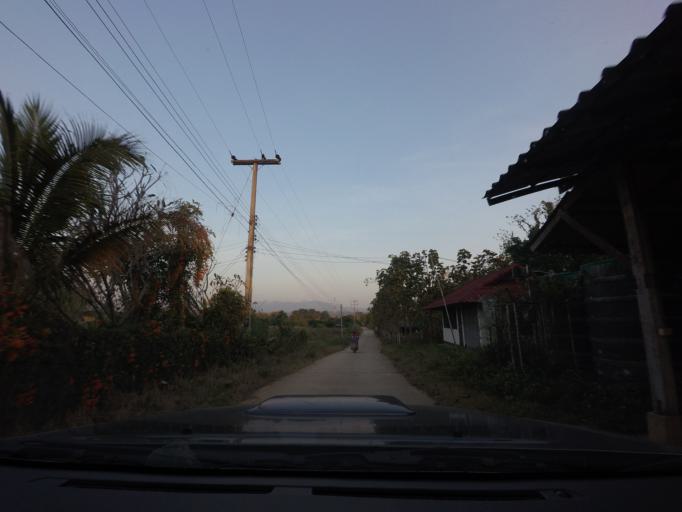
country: TH
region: Chiang Mai
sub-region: Amphoe Chiang Dao
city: Chiang Dao
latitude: 19.3683
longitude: 98.9546
